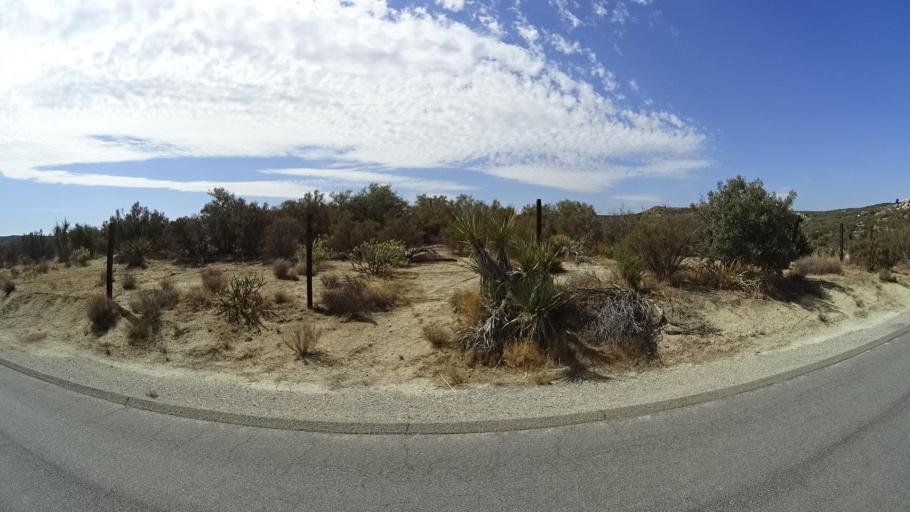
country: MX
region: Baja California
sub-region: Tecate
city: Cereso del Hongo
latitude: 32.6700
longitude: -116.2600
